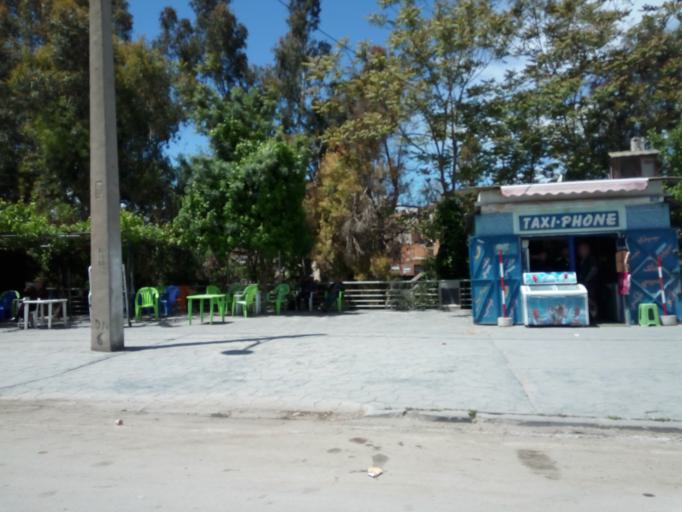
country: DZ
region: Constantine
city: Constantine
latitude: 36.3669
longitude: 6.6178
